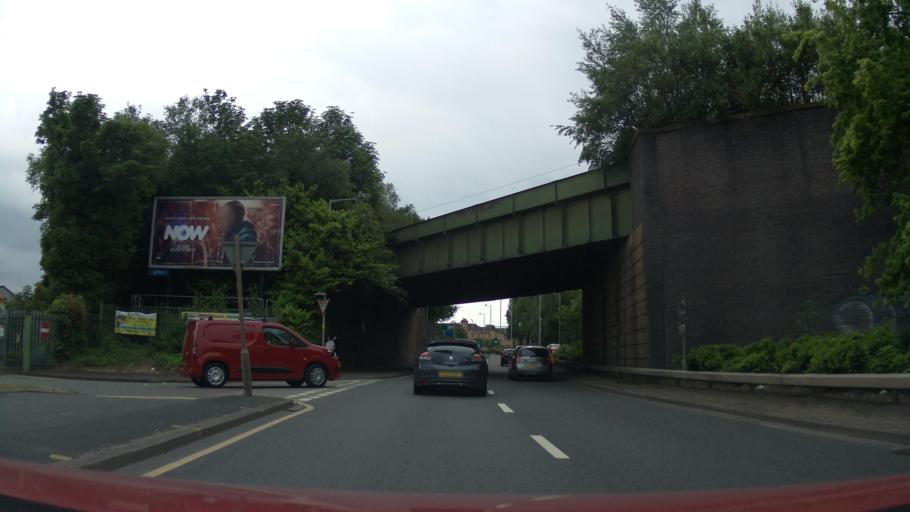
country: GB
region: England
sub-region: Wolverhampton
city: Wolverhampton
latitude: 52.5992
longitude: -2.1292
